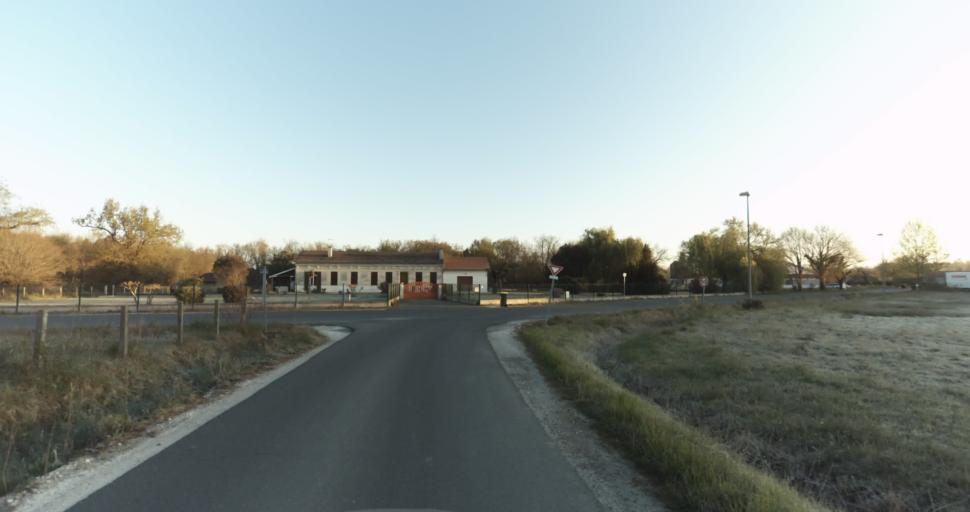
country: FR
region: Aquitaine
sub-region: Departement de la Gironde
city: Martignas-sur-Jalle
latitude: 44.8125
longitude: -0.7510
